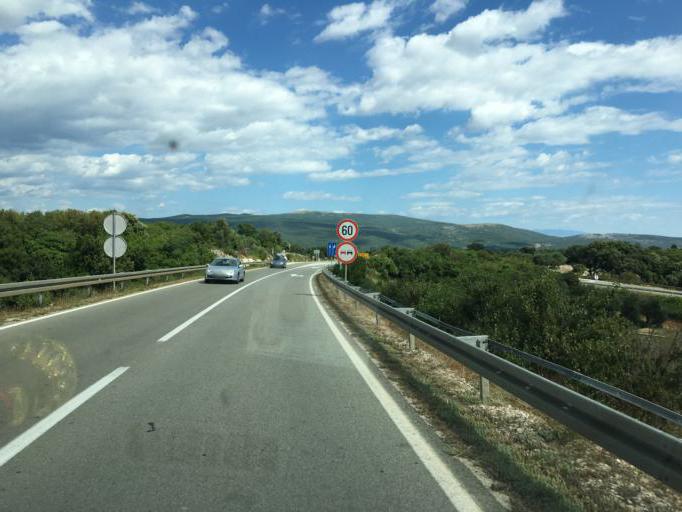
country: HR
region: Primorsko-Goranska
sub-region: Grad Krk
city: Krk
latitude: 45.0321
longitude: 14.5910
